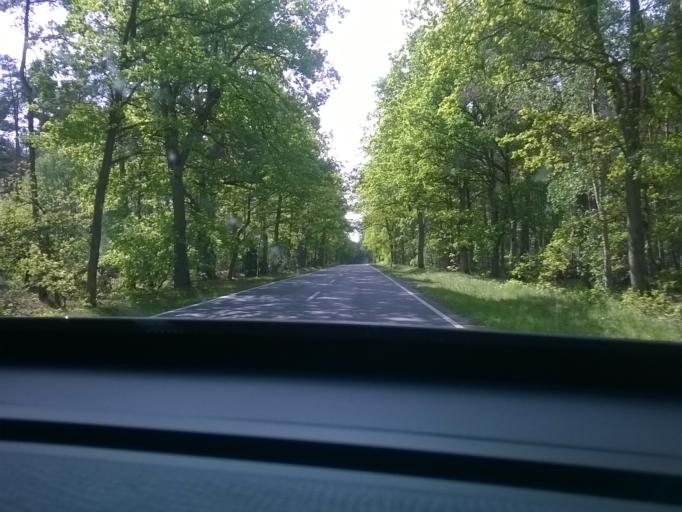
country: DE
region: Brandenburg
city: Wittstock
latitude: 53.1103
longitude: 12.4852
